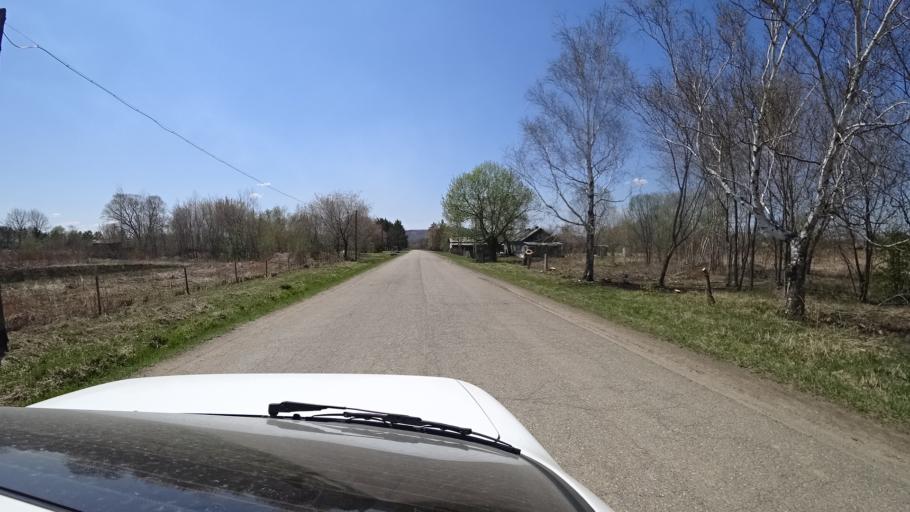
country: RU
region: Primorskiy
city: Dal'nerechensk
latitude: 45.7974
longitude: 133.7694
